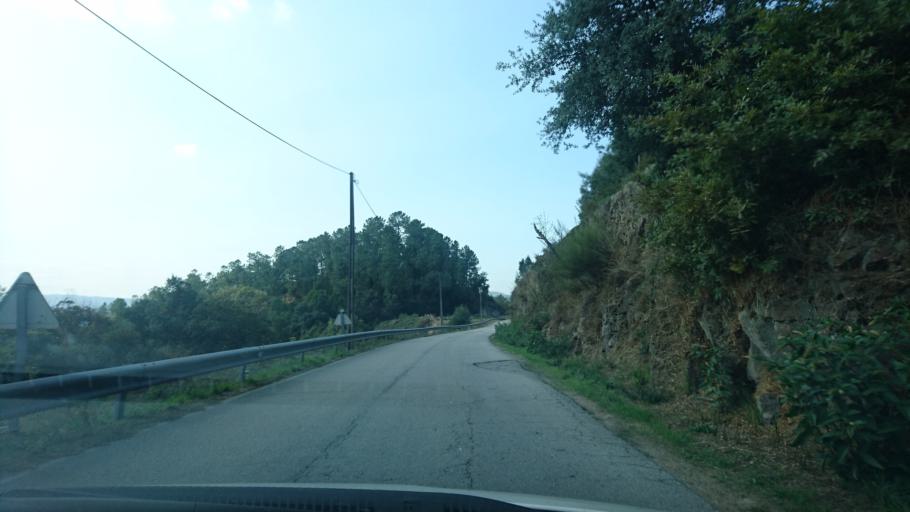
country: PT
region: Vila Real
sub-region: Mondim de Basto
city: Mondim de Basto
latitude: 41.4545
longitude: -7.9212
